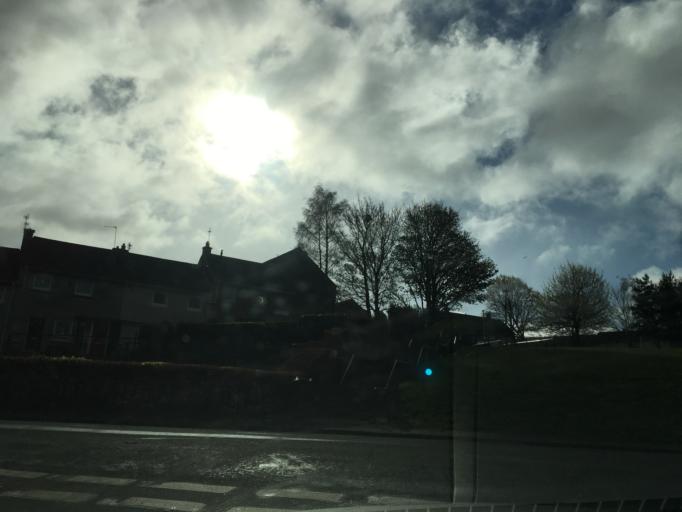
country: GB
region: Scotland
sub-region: Edinburgh
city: Colinton
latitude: 55.9054
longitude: -3.2301
